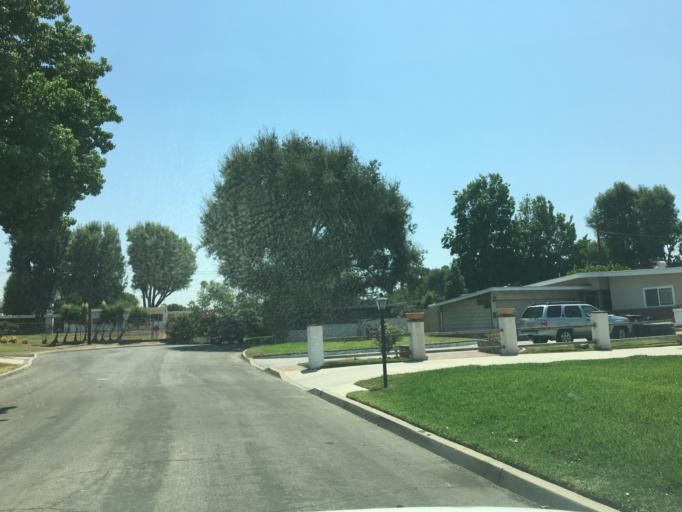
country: US
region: California
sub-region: Los Angeles County
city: Citrus
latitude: 34.1260
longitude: -117.8799
